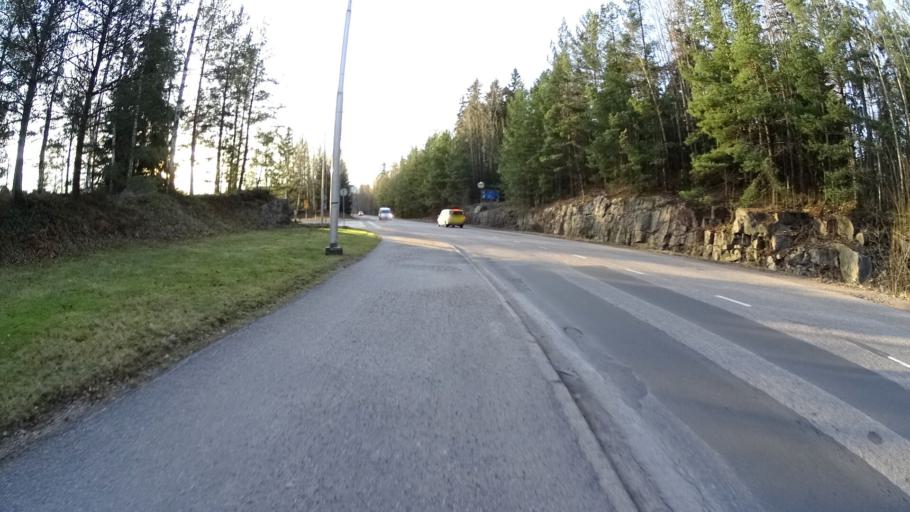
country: FI
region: Uusimaa
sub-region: Helsinki
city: Helsinki
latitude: 60.2163
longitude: 24.9179
